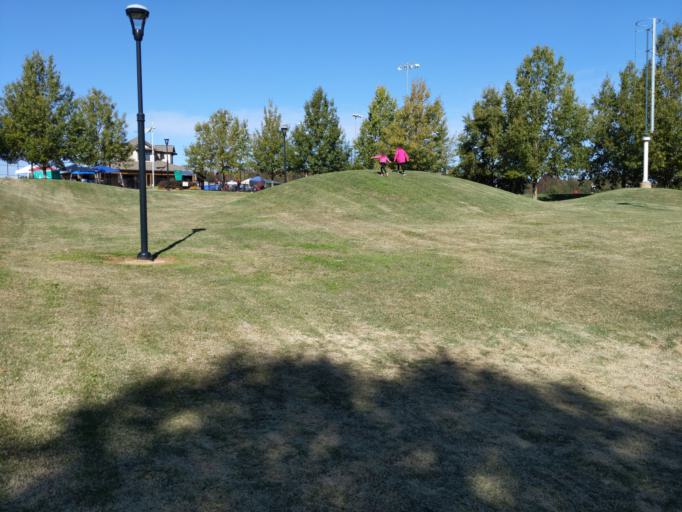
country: US
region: South Carolina
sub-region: Spartanburg County
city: Duncan
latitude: 34.8714
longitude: -82.1043
